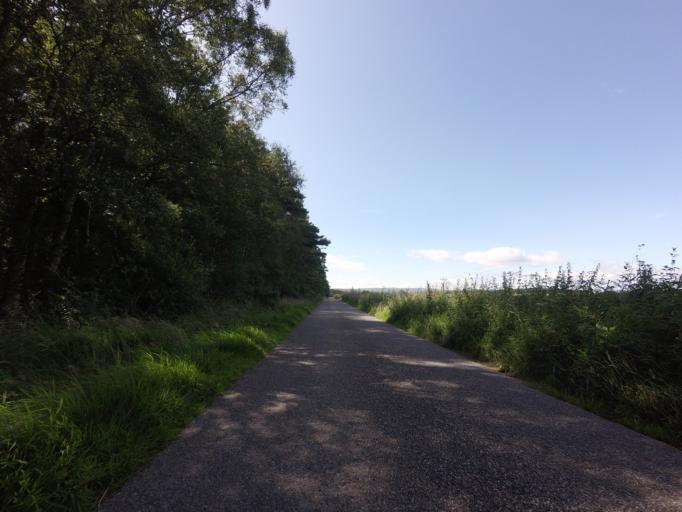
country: GB
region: Scotland
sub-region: Highland
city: Nairn
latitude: 57.5256
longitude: -3.8632
